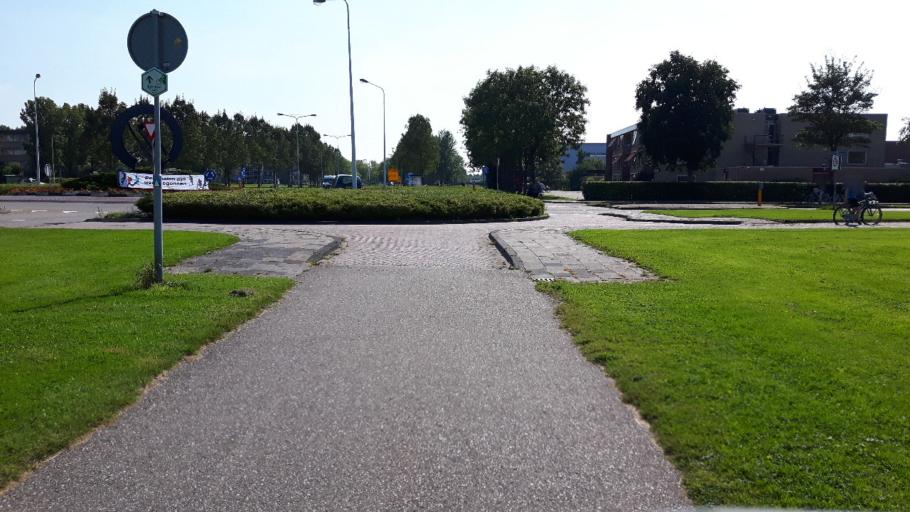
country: NL
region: Friesland
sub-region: Gemeente Franekeradeel
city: Franeker
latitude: 53.1962
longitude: 5.5407
